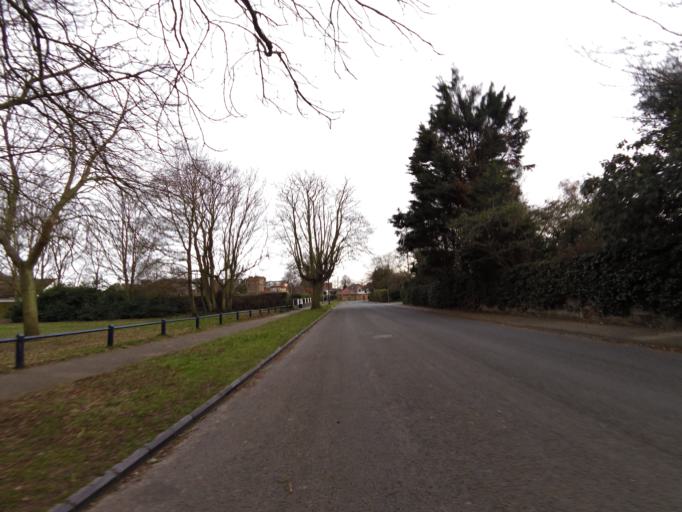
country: GB
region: England
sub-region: Suffolk
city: Felixstowe
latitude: 51.9680
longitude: 1.3714
